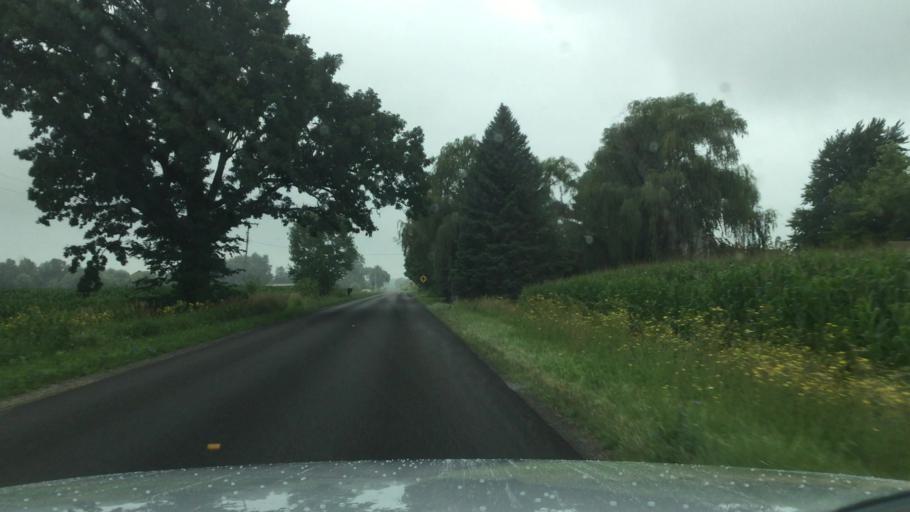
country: US
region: Michigan
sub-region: Shiawassee County
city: New Haven
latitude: 43.0573
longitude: -84.1453
